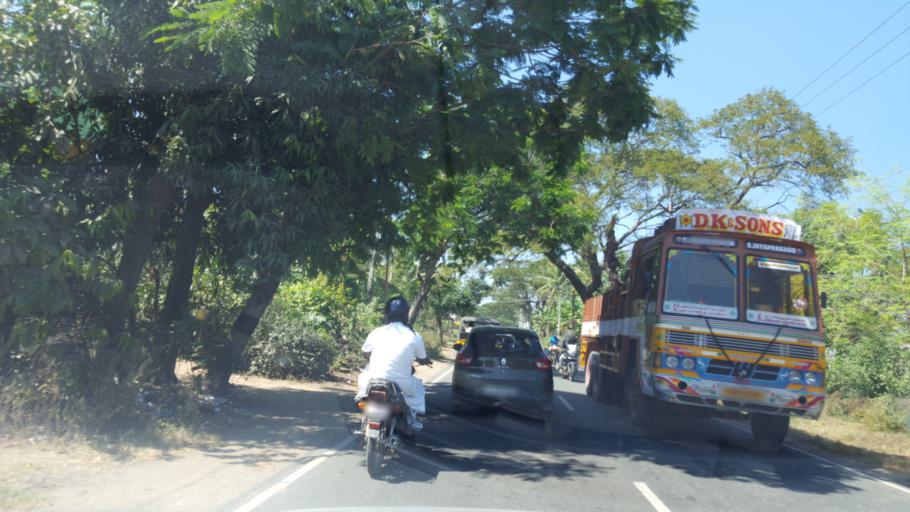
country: IN
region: Tamil Nadu
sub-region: Kancheepuram
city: Chengalpattu
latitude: 12.7112
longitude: 79.9606
